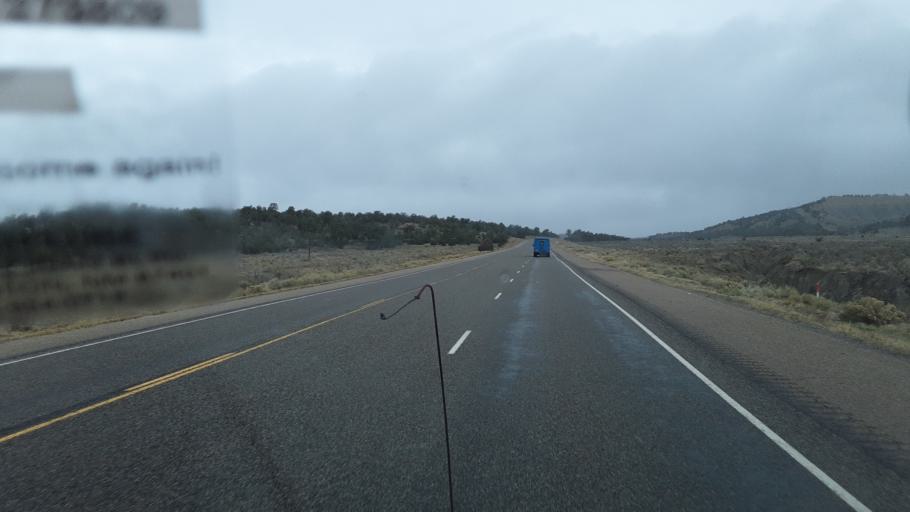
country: US
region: New Mexico
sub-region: Rio Arriba County
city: Tierra Amarilla
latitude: 36.4470
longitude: -106.4755
